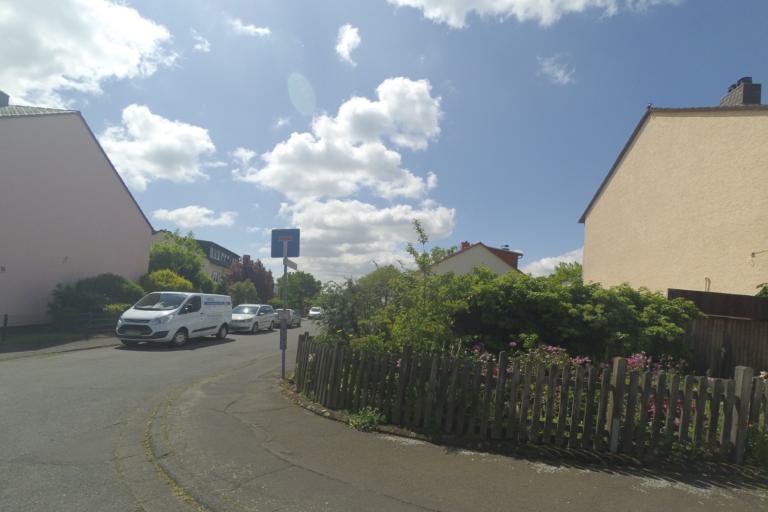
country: DE
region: Hesse
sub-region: Regierungsbezirk Darmstadt
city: Rosbach vor der Hohe
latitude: 50.2610
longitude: 8.6970
